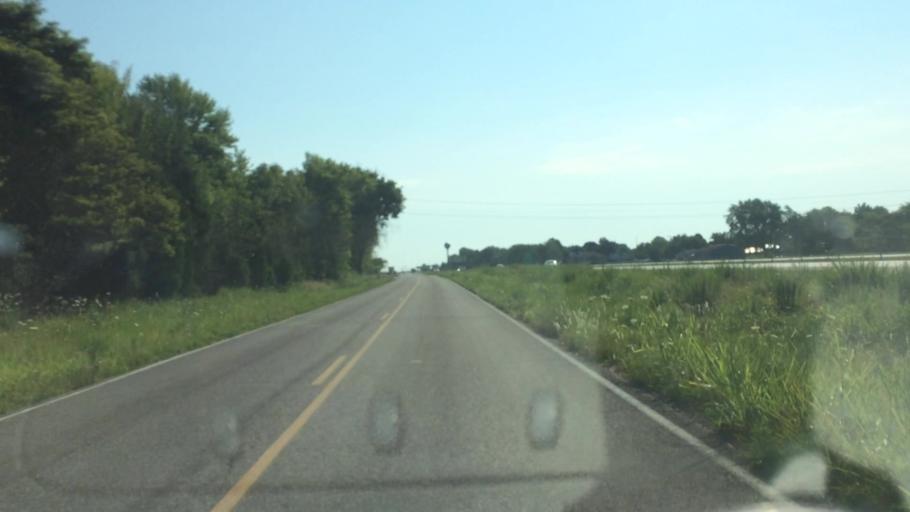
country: US
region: Missouri
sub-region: Greene County
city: Strafford
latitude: 37.2662
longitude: -93.1378
